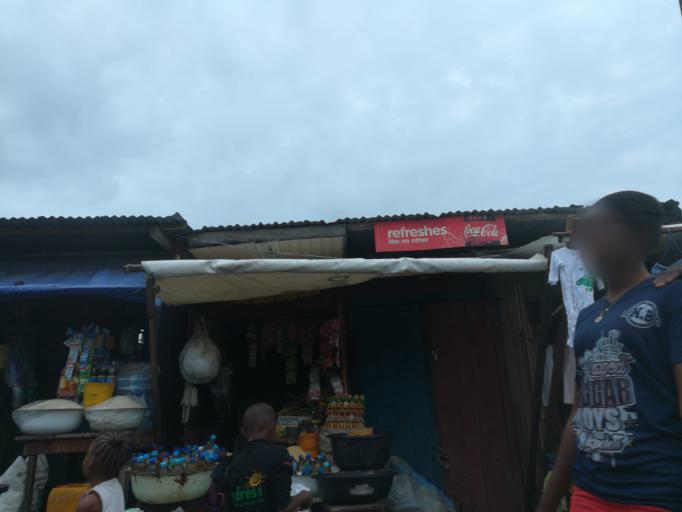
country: NG
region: Lagos
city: Makoko
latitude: 6.4950
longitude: 3.3858
